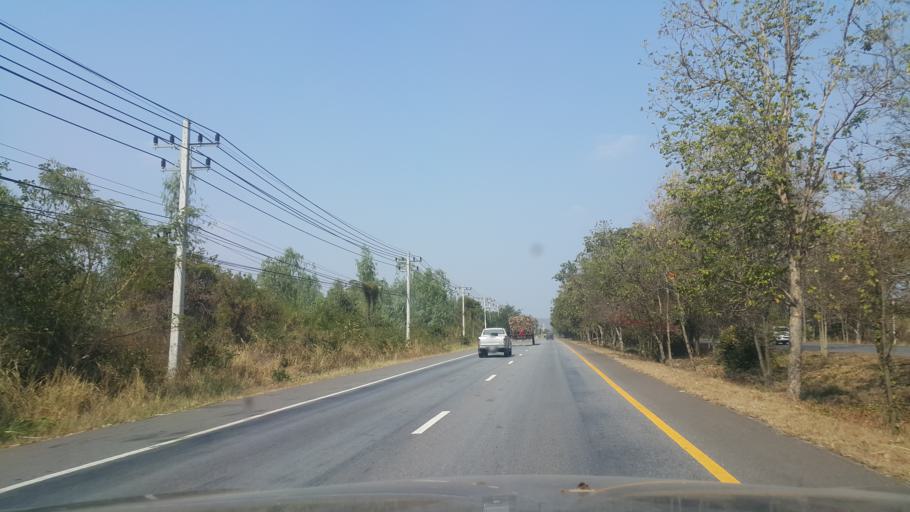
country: TH
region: Nakhon Ratchasima
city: Wang Nam Khiao
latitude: 14.5422
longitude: 101.9700
